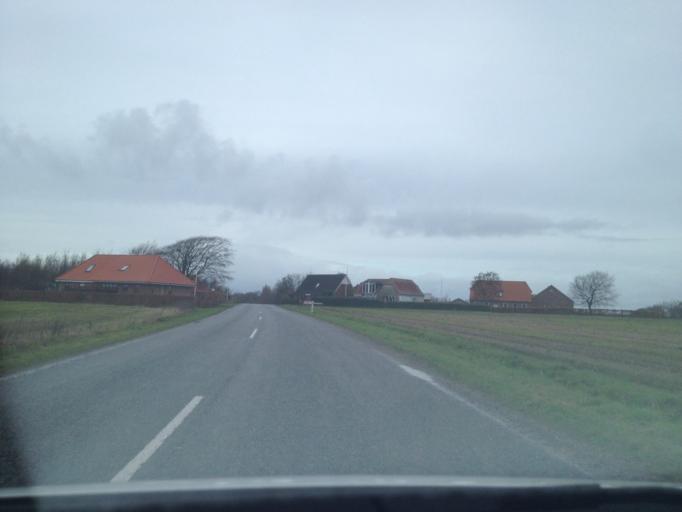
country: DK
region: South Denmark
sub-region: Tonder Kommune
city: Sherrebek
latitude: 55.2381
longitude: 8.8338
